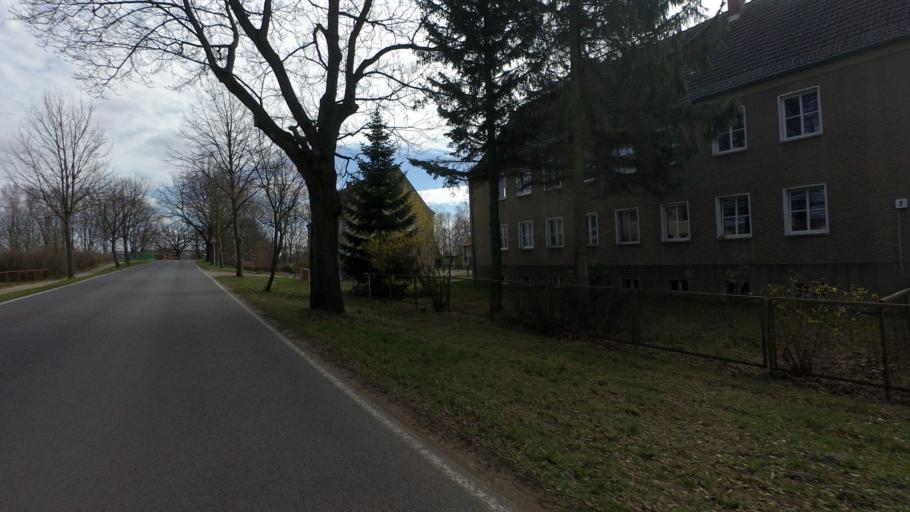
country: DE
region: Berlin
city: Blankenfelde
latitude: 52.6571
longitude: 13.4278
